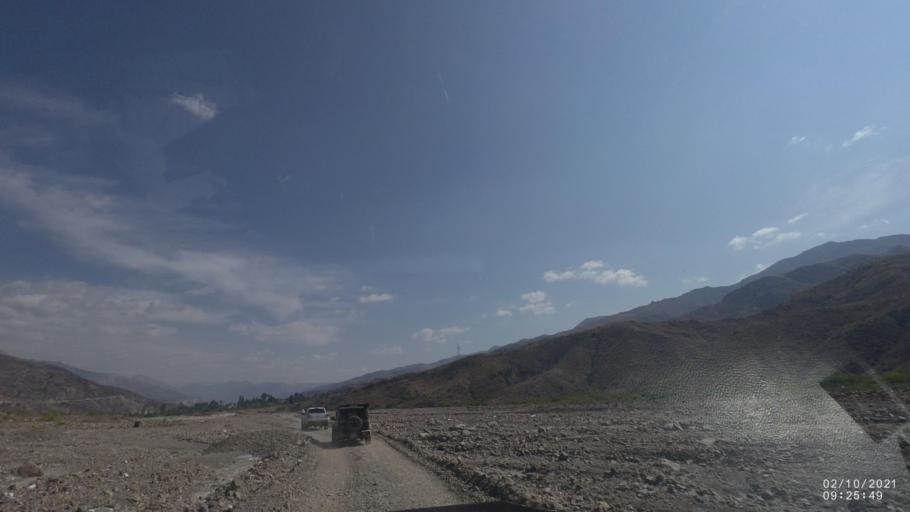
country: BO
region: Cochabamba
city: Irpa Irpa
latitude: -17.8606
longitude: -66.3128
